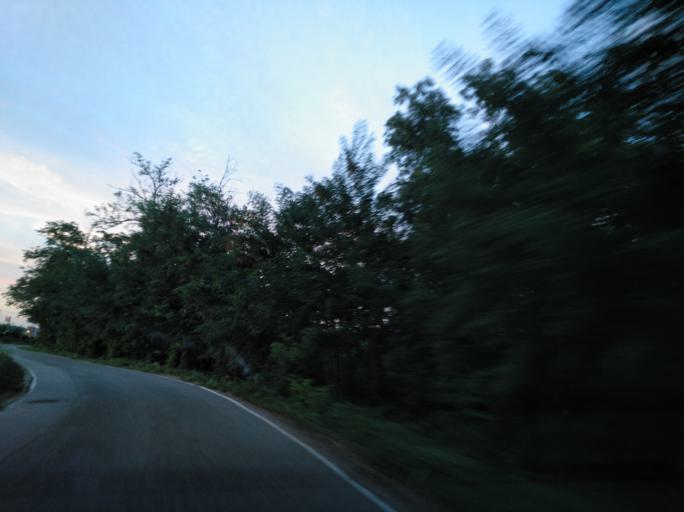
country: ES
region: Catalonia
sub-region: Provincia de Girona
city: Salt
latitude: 41.9585
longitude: 2.7945
